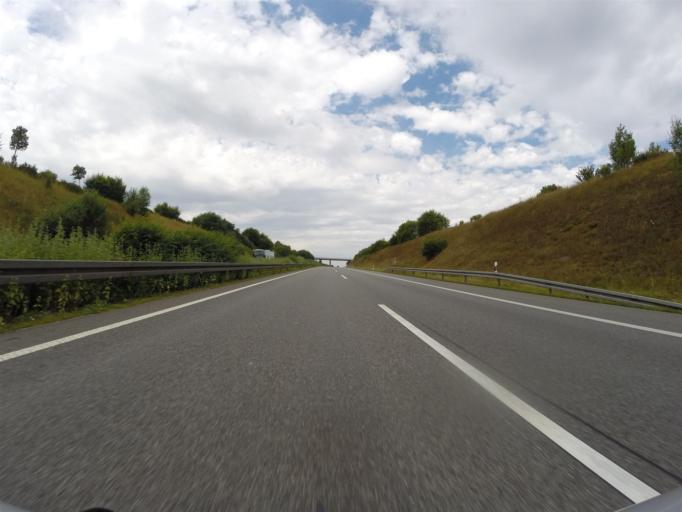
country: DE
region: Thuringia
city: Hausen
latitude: 51.3968
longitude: 10.3701
